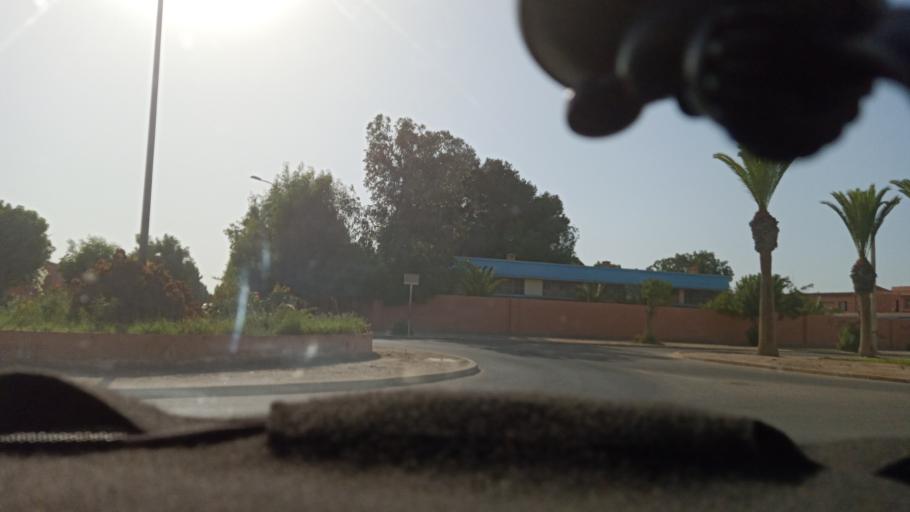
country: MA
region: Doukkala-Abda
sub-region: Safi
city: Youssoufia
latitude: 32.2466
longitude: -8.5264
